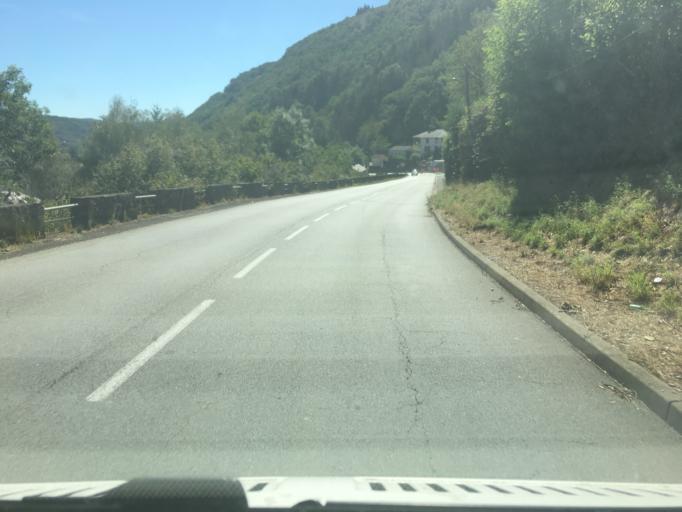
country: FR
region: Limousin
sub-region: Departement de la Correze
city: Bort-les-Orgues
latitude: 45.4036
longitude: 2.4960
